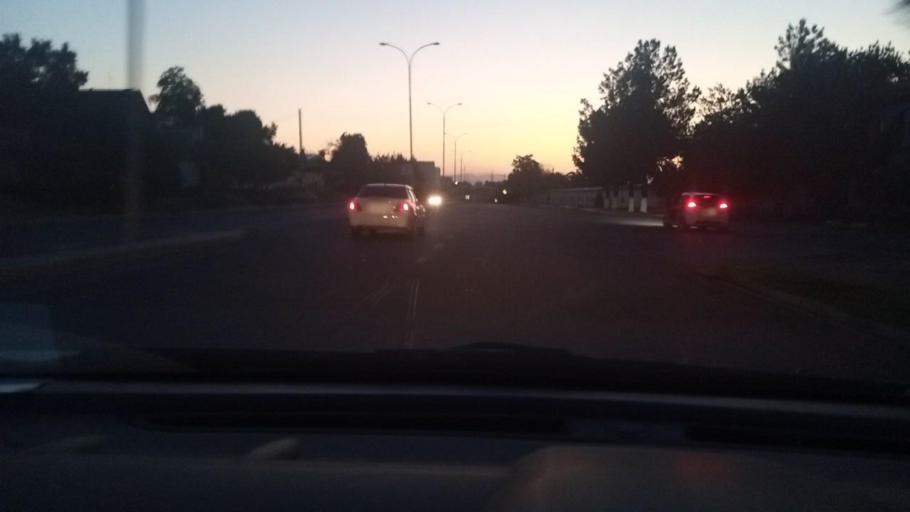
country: UZ
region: Toshkent Shahri
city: Tashkent
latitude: 41.2507
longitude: 69.2128
